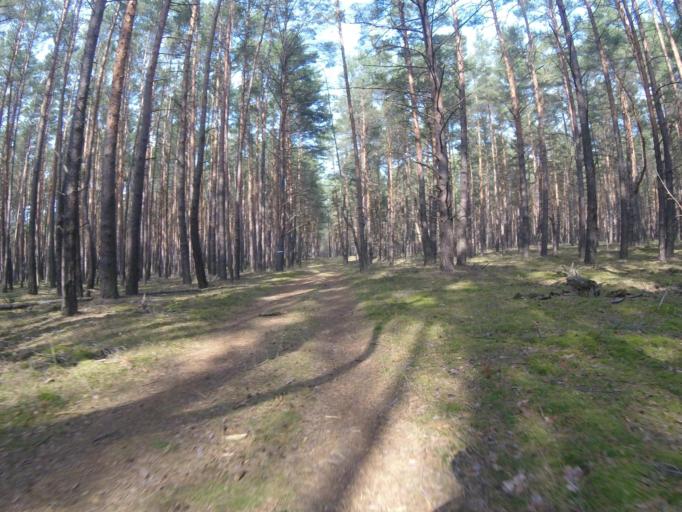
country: DE
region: Brandenburg
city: Bestensee
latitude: 52.2536
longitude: 13.6845
